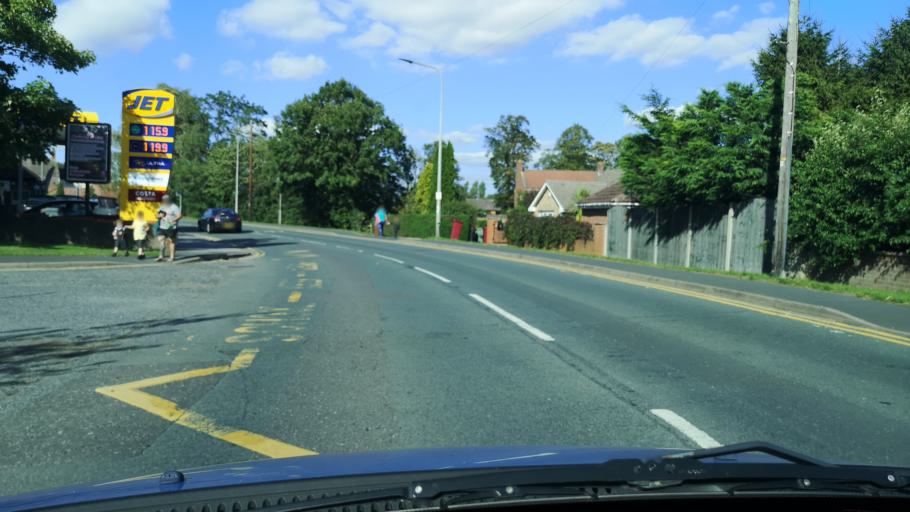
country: GB
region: England
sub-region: North Lincolnshire
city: Belton
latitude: 53.5553
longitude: -0.8156
